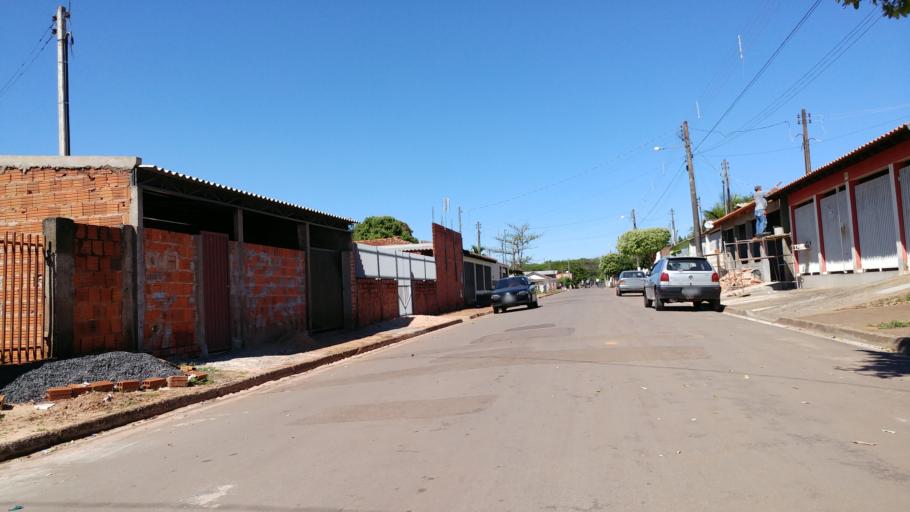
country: BR
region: Sao Paulo
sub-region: Paraguacu Paulista
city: Paraguacu Paulista
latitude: -22.4174
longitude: -50.5678
